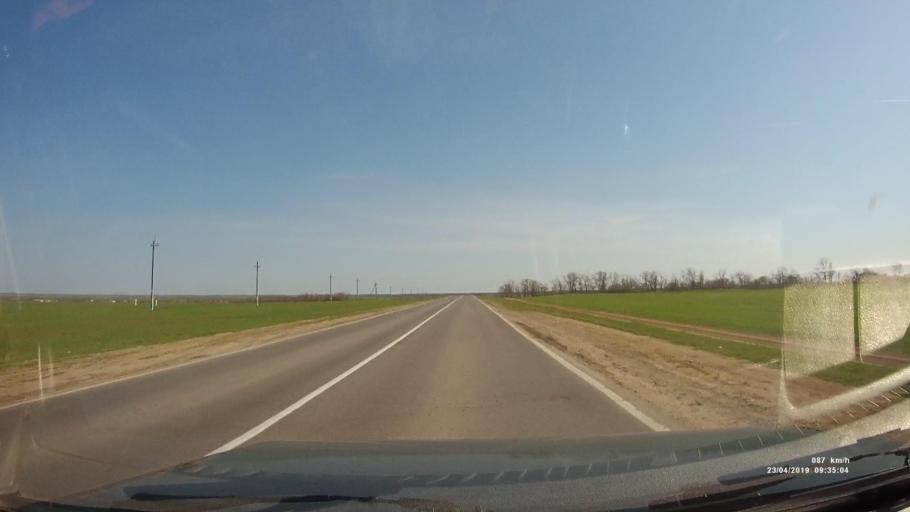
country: RU
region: Rostov
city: Gundorovskiy
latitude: 46.8180
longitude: 41.8654
